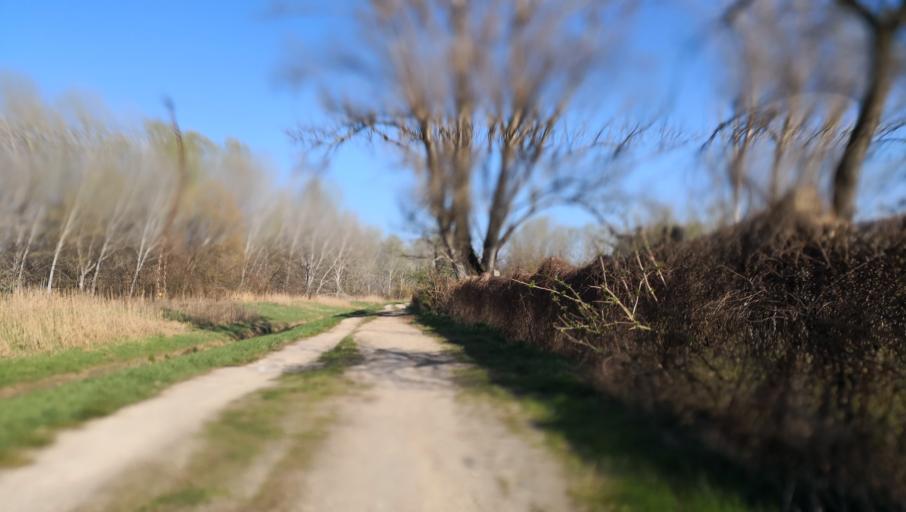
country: HU
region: Budapest
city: Budapest XVII. keruelet
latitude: 47.4873
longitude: 19.2332
